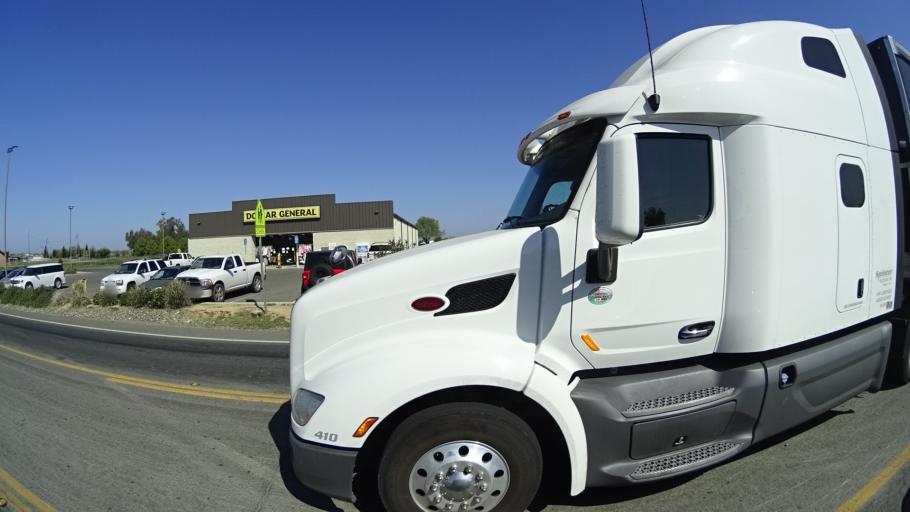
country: US
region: California
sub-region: Glenn County
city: Hamilton City
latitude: 39.7458
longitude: -122.0149
